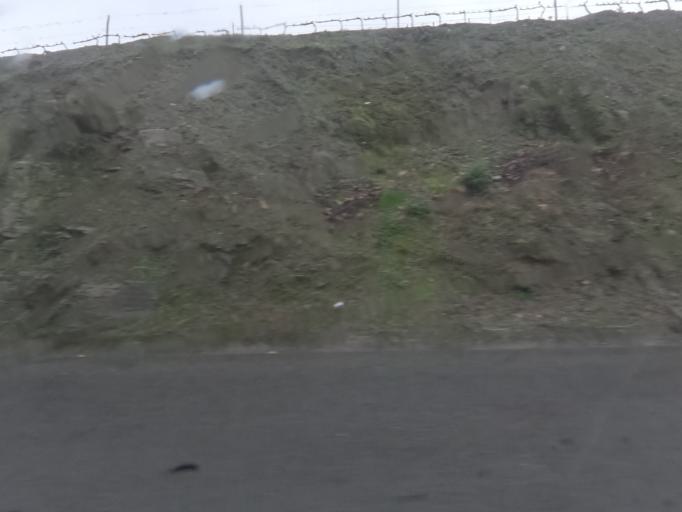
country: PT
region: Vila Real
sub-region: Peso da Regua
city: Peso da Regua
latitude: 41.1717
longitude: -7.7618
